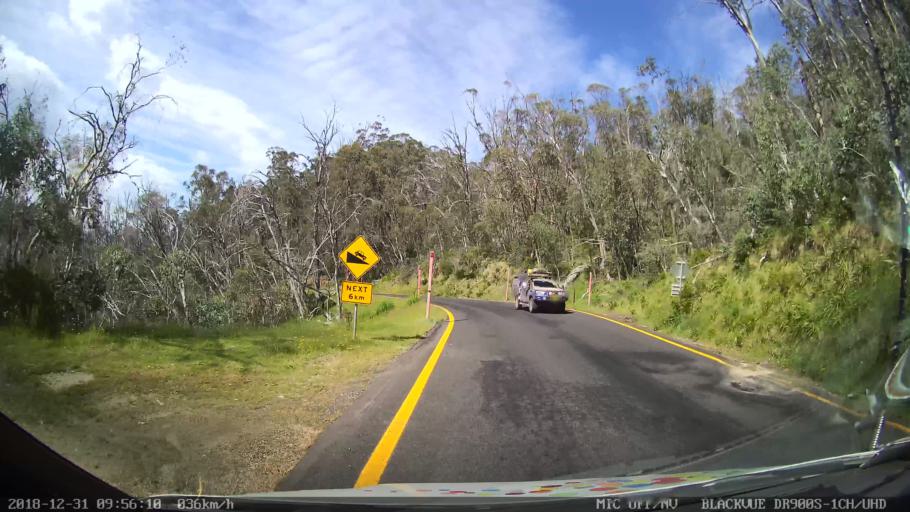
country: AU
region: New South Wales
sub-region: Snowy River
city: Jindabyne
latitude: -36.5301
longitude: 148.2256
